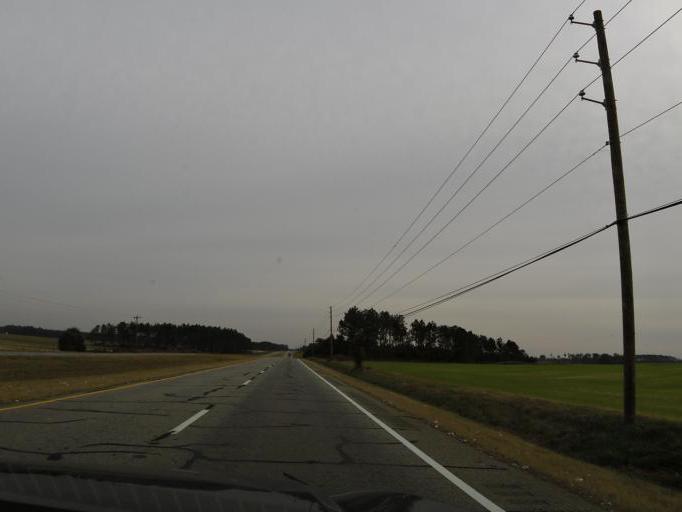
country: US
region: Georgia
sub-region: Decatur County
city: Bainbridge
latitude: 30.9655
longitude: -84.7258
